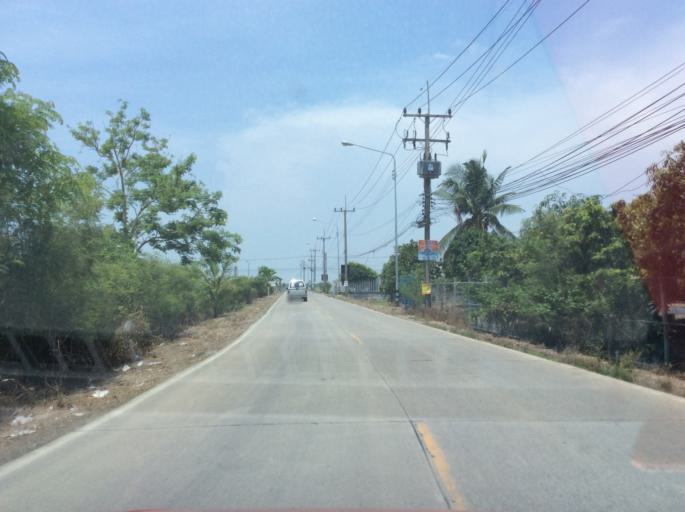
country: TH
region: Pathum Thani
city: Ban Lam Luk Ka
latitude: 13.9856
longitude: 100.7758
